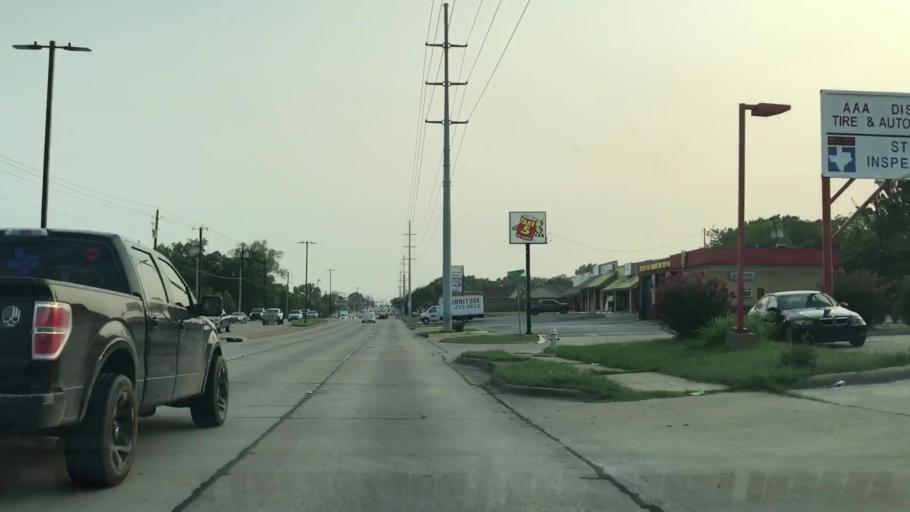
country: US
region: Texas
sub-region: Dallas County
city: Garland
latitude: 32.8653
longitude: -96.6377
